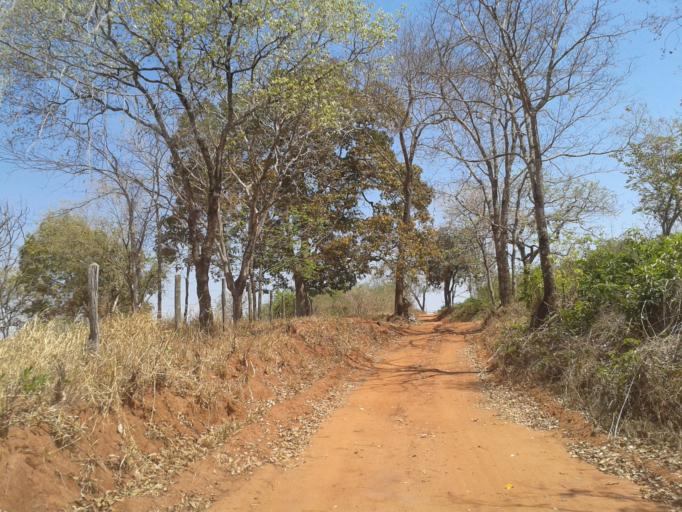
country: BR
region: Minas Gerais
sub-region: Ituiutaba
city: Ituiutaba
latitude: -19.0994
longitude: -49.3003
